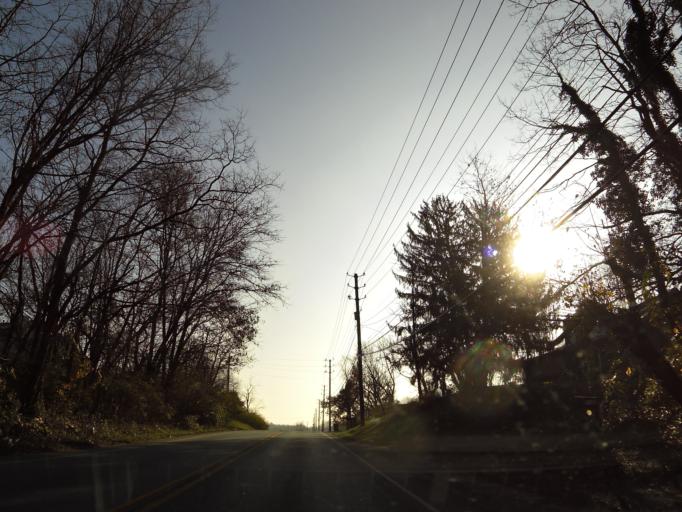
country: US
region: Indiana
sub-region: Marion County
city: Clermont
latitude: 39.8067
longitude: -86.2972
